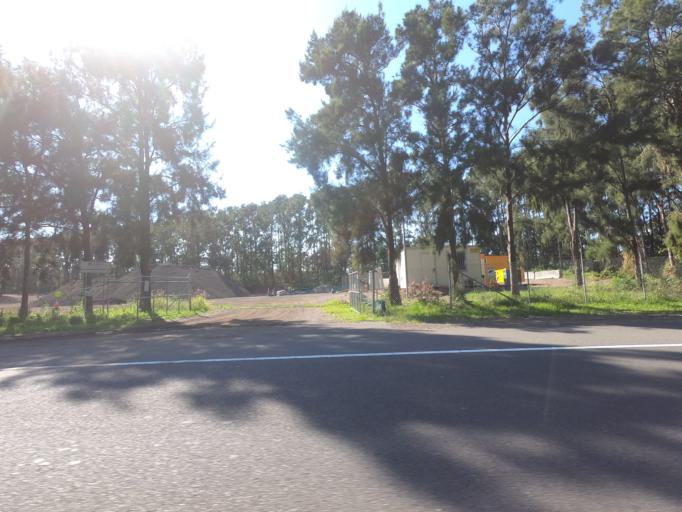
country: AU
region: New South Wales
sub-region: Wollongong
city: Mount Saint Thomas
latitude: -34.4574
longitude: 150.8546
